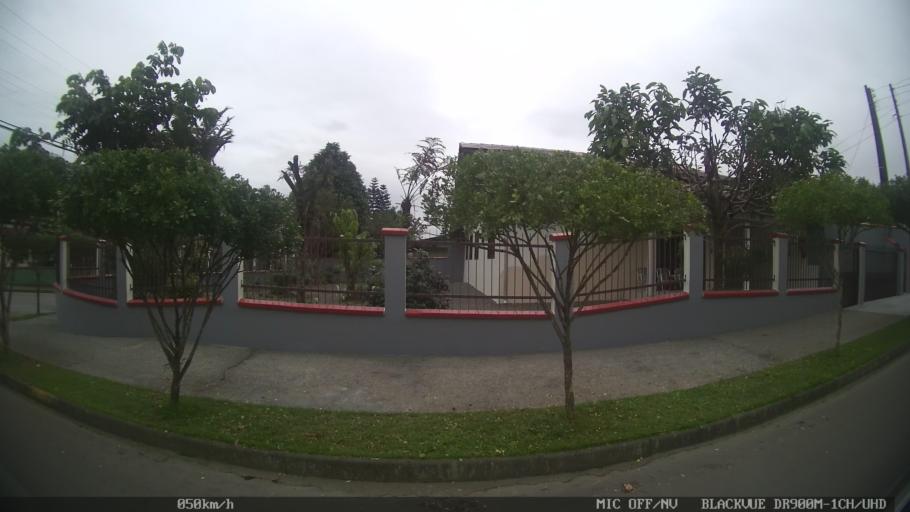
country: BR
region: Santa Catarina
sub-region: Joinville
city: Joinville
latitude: -26.2720
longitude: -48.8902
